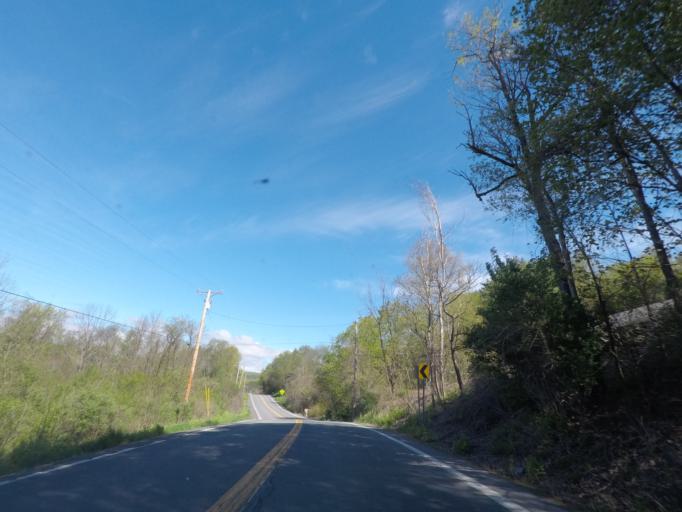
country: US
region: New York
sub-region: Albany County
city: Ravena
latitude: 42.5020
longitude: -73.9463
